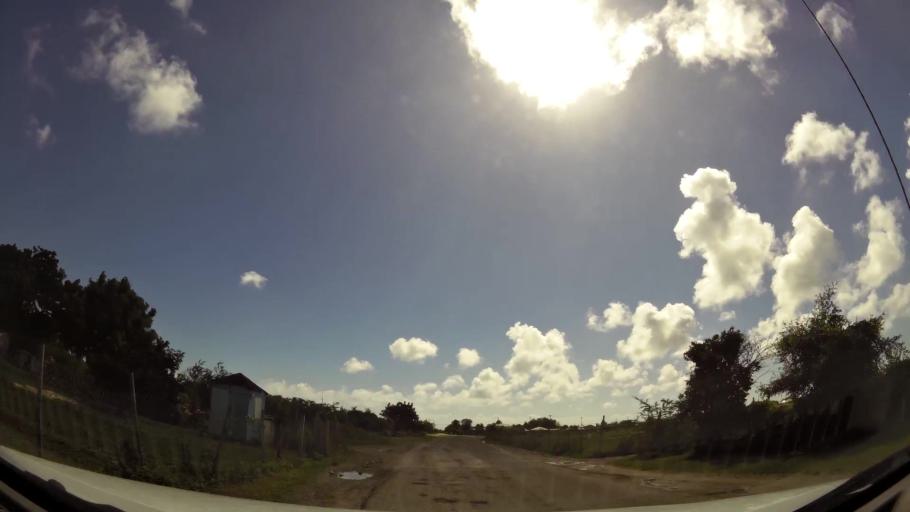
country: AG
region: Barbuda
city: Codrington
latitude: 17.6368
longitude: -61.8230
